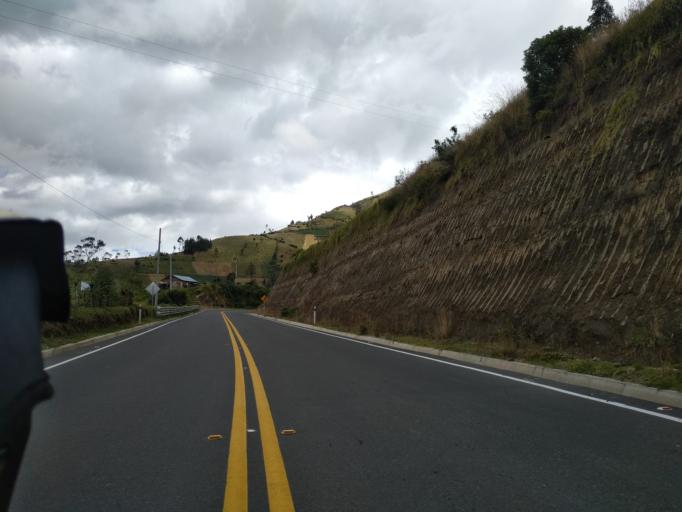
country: EC
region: Cotopaxi
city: Saquisili
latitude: -0.7625
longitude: -78.9079
